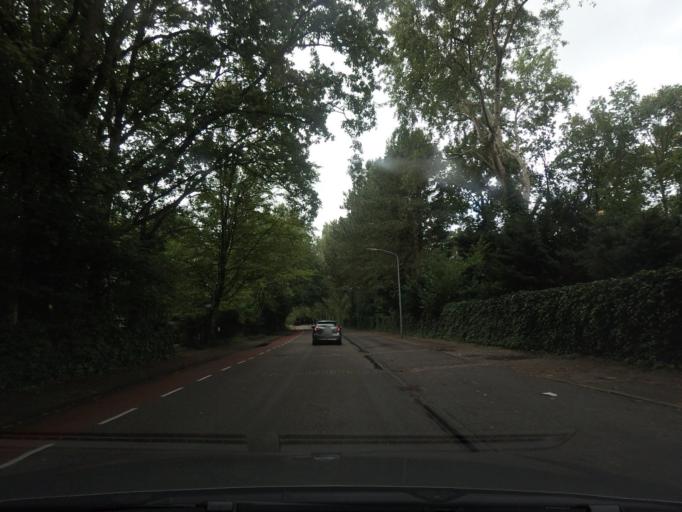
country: NL
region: North Holland
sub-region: Gemeente Heemstede
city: Heemstede
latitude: 52.3552
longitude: 4.5882
